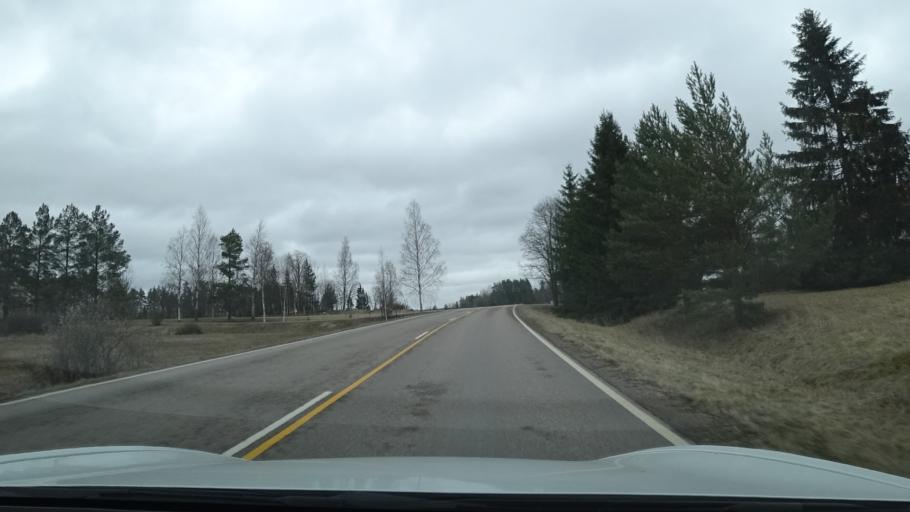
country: FI
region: Uusimaa
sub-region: Porvoo
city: Myrskylae
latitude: 60.6811
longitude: 25.8881
